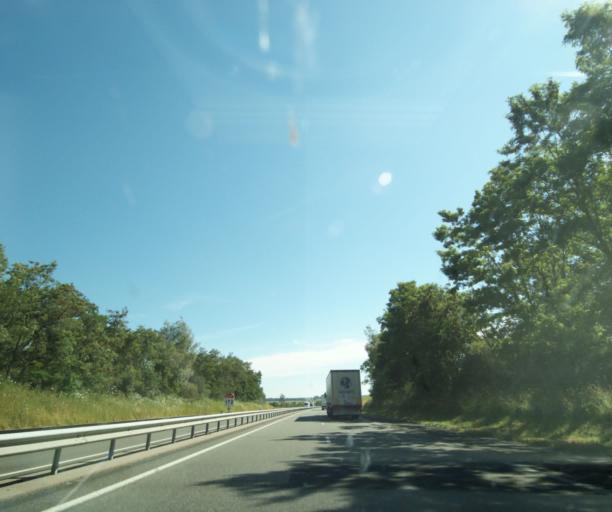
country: FR
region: Lorraine
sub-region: Departement des Vosges
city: Bulgneville
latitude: 48.2004
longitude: 5.7916
